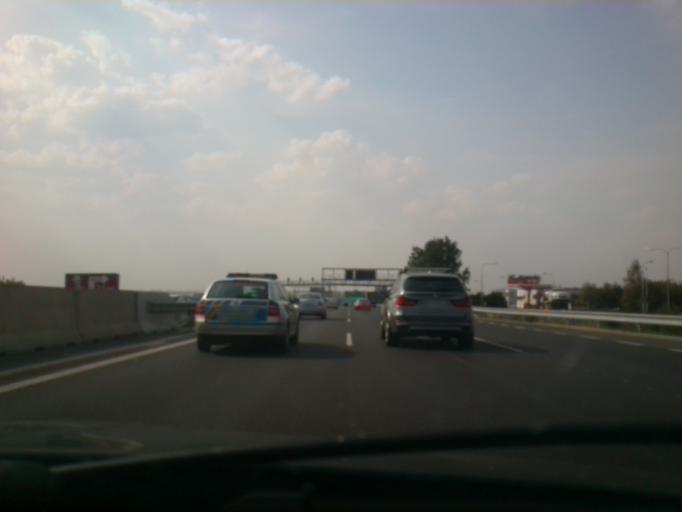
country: CZ
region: Central Bohemia
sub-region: Okres Praha-Zapad
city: Pruhonice
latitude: 49.9955
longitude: 14.5839
